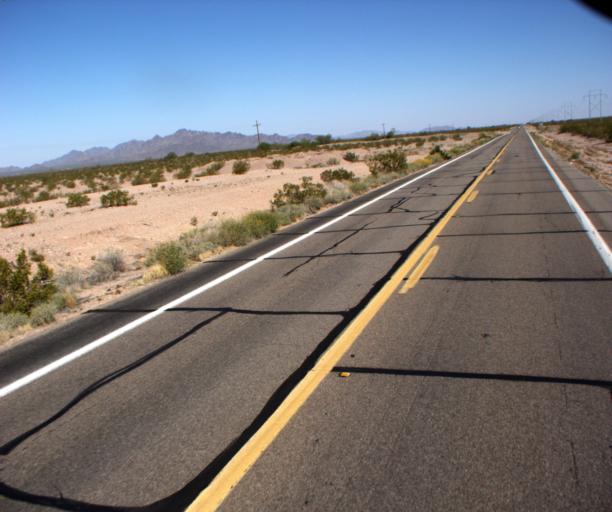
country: US
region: Arizona
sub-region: La Paz County
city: Quartzsite
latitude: 33.4133
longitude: -114.2170
